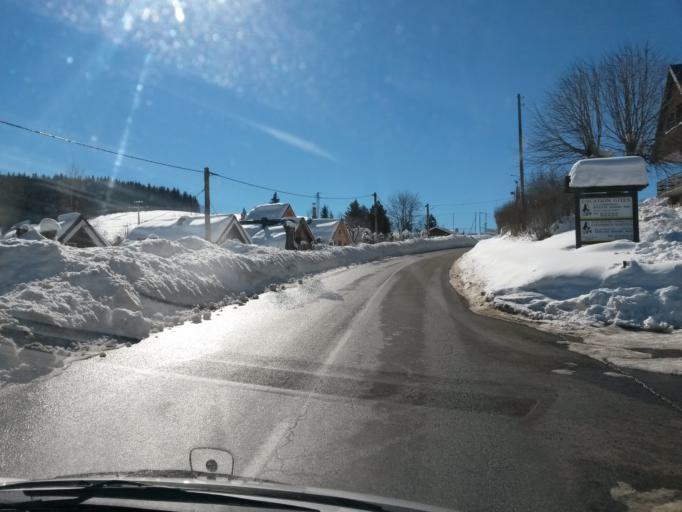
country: FR
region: Rhone-Alpes
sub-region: Departement de l'Isere
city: Saint-Hilaire
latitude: 45.3041
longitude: 5.8797
